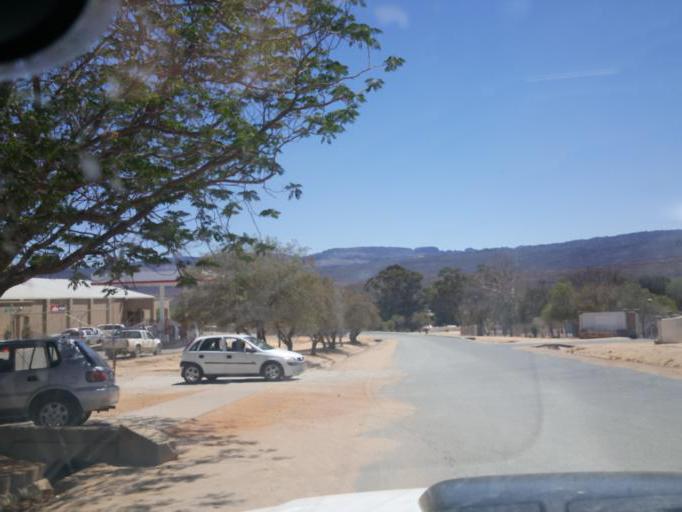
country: ZA
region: Western Cape
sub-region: West Coast District Municipality
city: Clanwilliam
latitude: -32.1889
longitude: 18.8889
